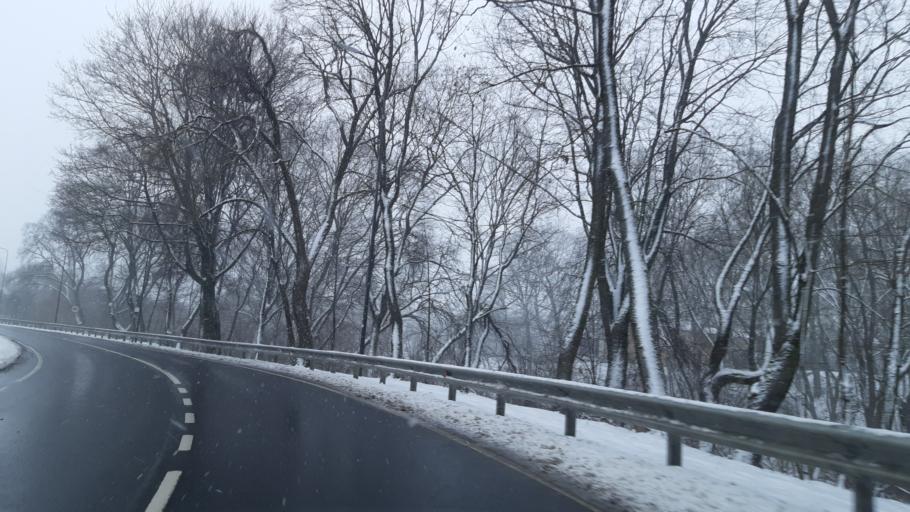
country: LT
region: Kauno apskritis
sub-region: Kaunas
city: Silainiai
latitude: 54.9307
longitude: 23.8709
